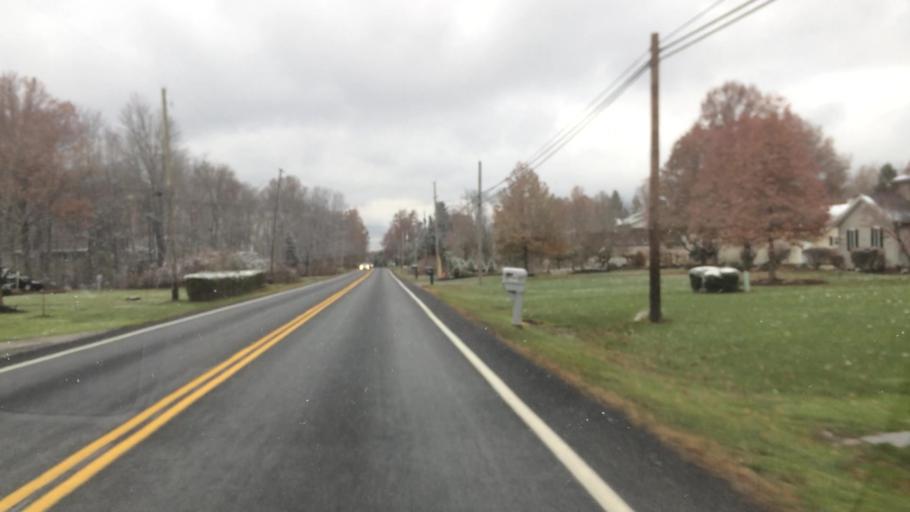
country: US
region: Ohio
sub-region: Summit County
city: Boston Heights
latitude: 41.2866
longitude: -81.5177
